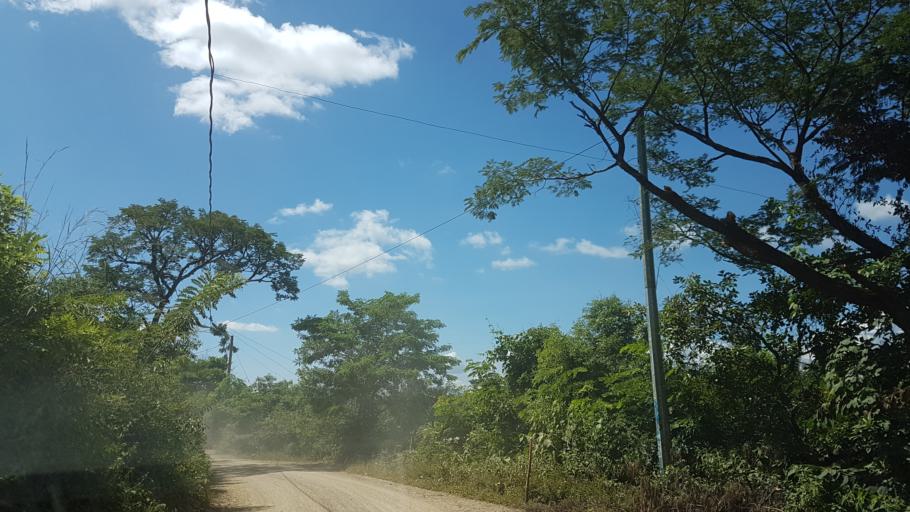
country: HN
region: El Paraiso
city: Santa Cruz
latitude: 13.7324
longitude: -86.6894
